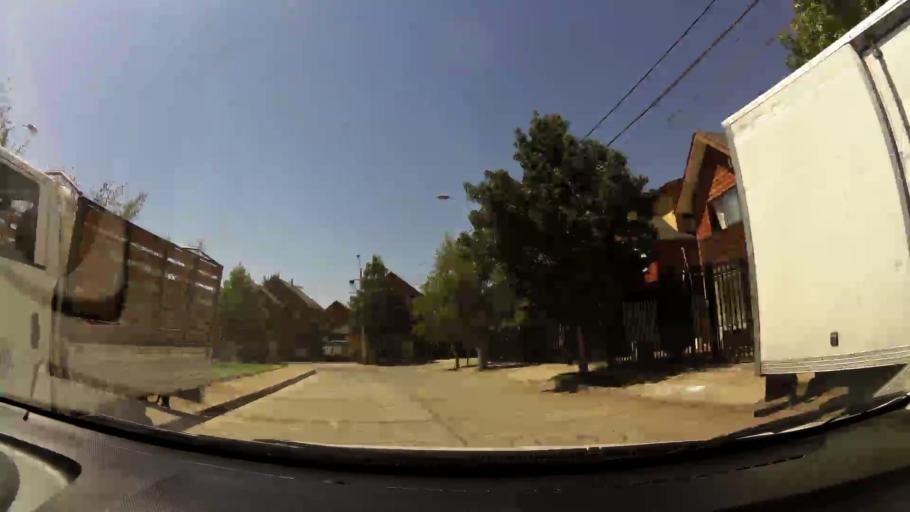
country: CL
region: Maule
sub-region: Provincia de Talca
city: Talca
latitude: -35.4268
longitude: -71.6113
